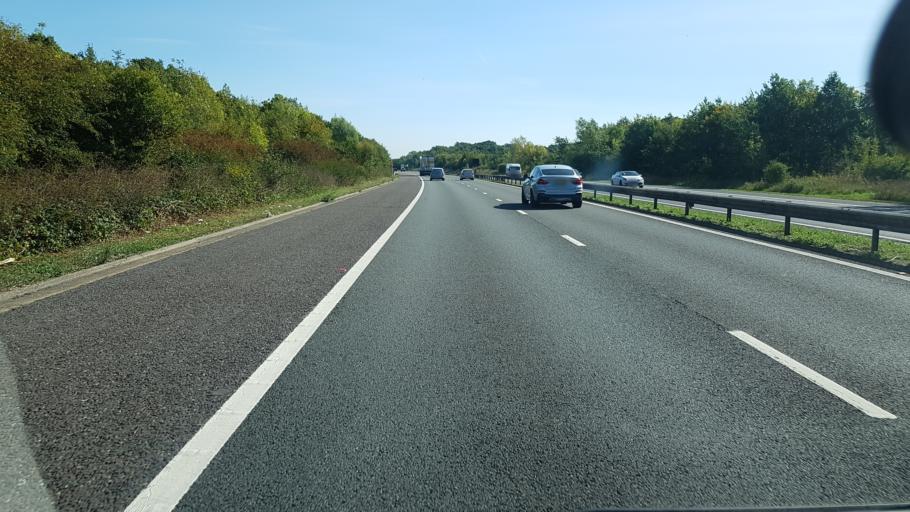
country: GB
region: England
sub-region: Kent
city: Borough Green
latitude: 51.3009
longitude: 0.3177
